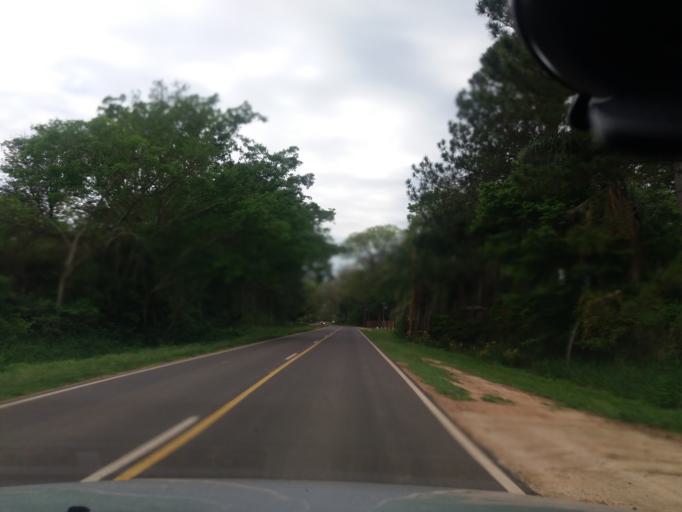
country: AR
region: Corrientes
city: Riachuelo
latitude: -27.4568
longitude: -58.6847
